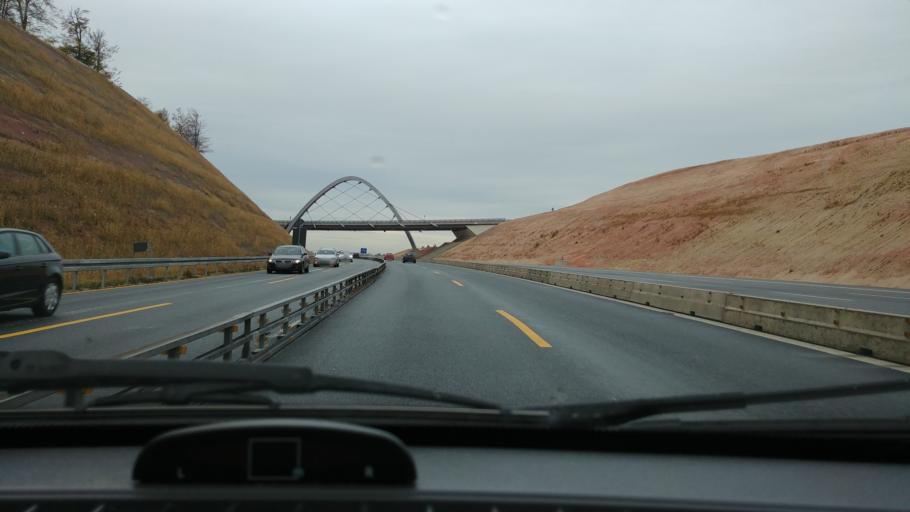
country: DE
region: Bavaria
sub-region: Regierungsbezirk Unterfranken
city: Altenbuch
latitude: 49.8895
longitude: 9.4124
